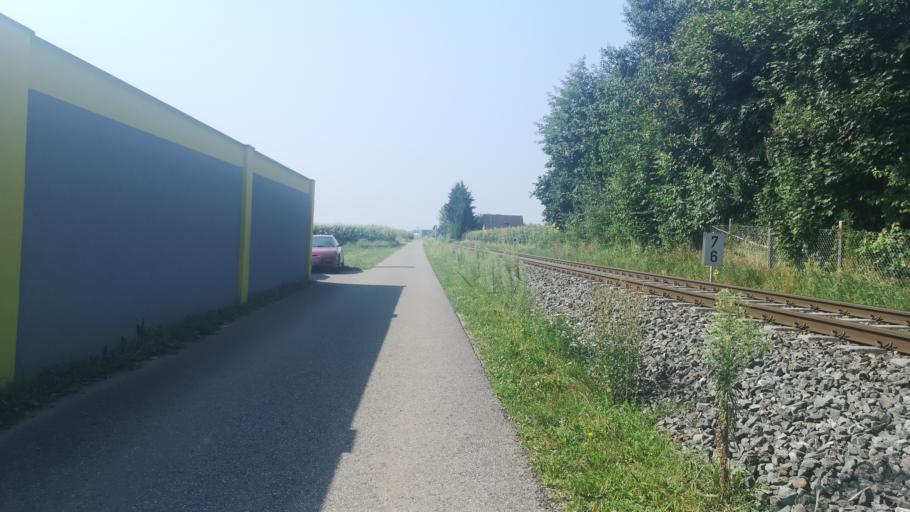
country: AT
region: Styria
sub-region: Politischer Bezirk Graz-Umgebung
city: Seiersberg
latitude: 47.0087
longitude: 15.4024
